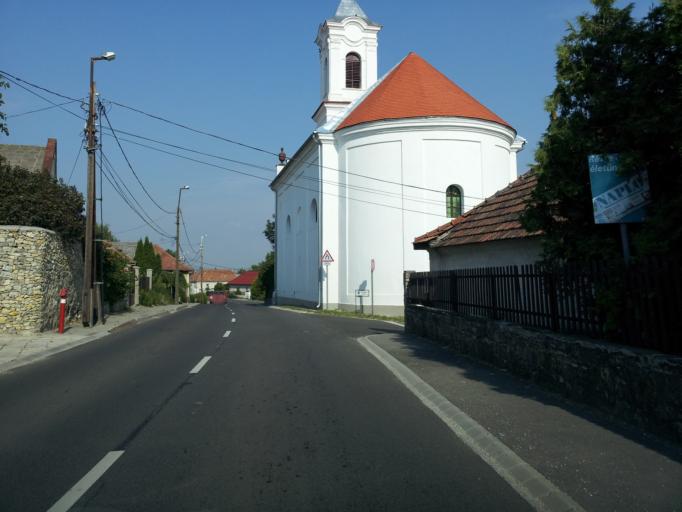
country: HU
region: Veszprem
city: Liter
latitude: 47.1092
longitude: 18.0425
